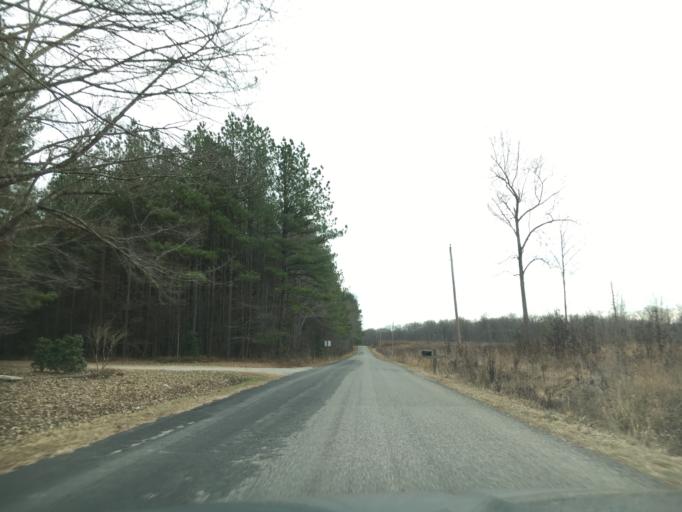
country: US
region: Virginia
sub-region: Amelia County
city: Amelia Court House
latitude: 37.4226
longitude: -77.9926
